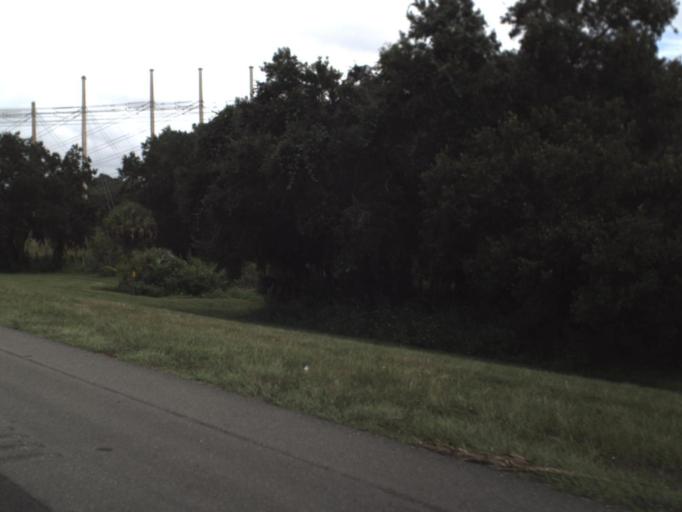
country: US
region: Florida
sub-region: Sarasota County
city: The Meadows
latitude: 27.4051
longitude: -82.4531
